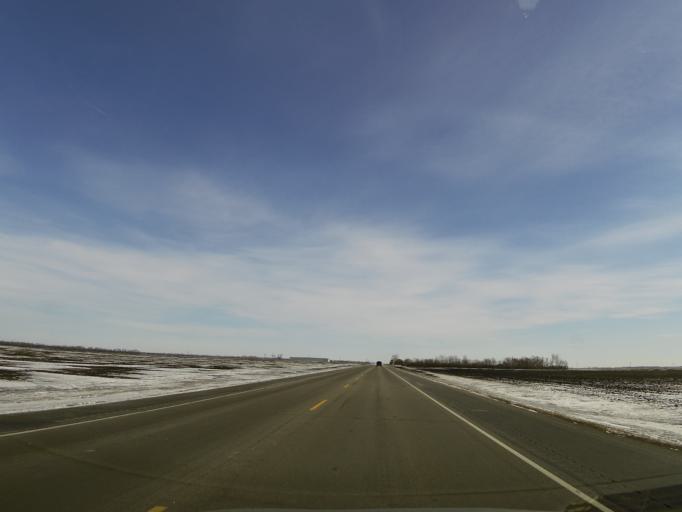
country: US
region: North Dakota
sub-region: Walsh County
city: Grafton
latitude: 48.4123
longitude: -97.3540
